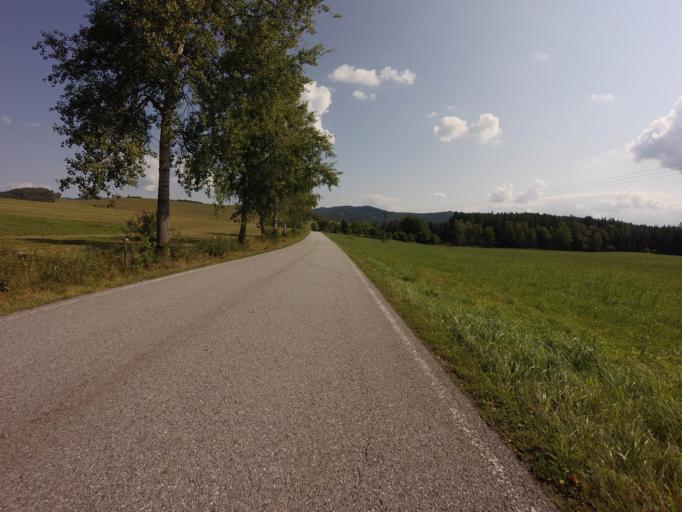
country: CZ
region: Jihocesky
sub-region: Okres Cesky Krumlov
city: Vyssi Brod
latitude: 48.6363
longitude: 14.3484
